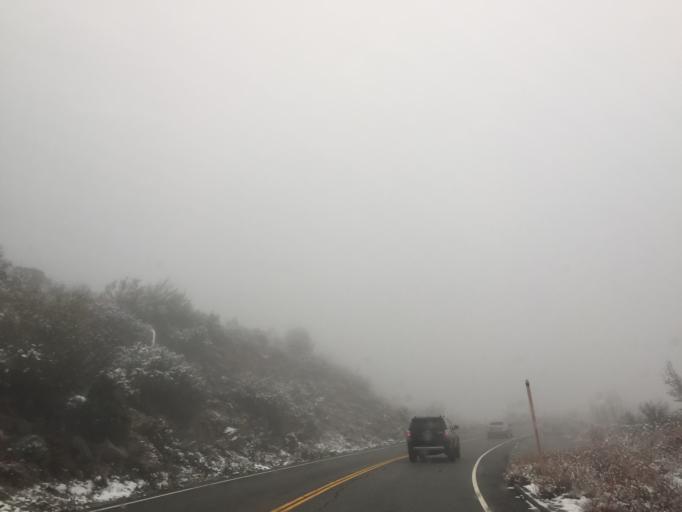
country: US
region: California
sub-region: Los Angeles County
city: Glendora
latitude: 34.3092
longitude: -117.8435
